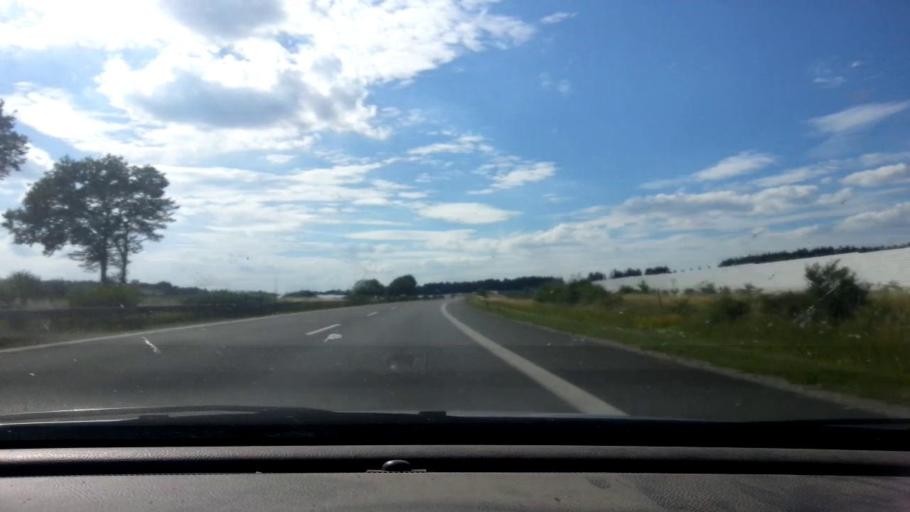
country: DE
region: Bavaria
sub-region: Upper Franconia
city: Wonsees
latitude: 50.0049
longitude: 11.2882
